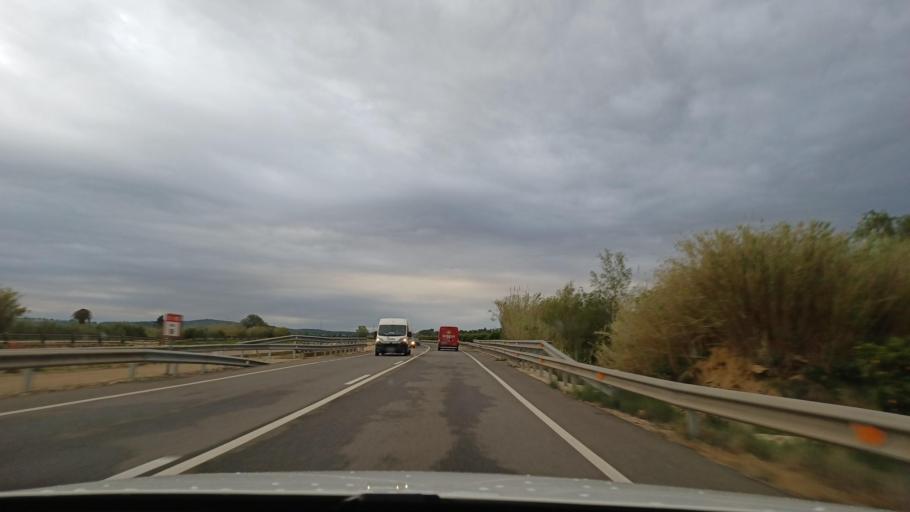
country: ES
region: Catalonia
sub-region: Provincia de Tarragona
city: Masdenverge
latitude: 40.7528
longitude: 0.5433
